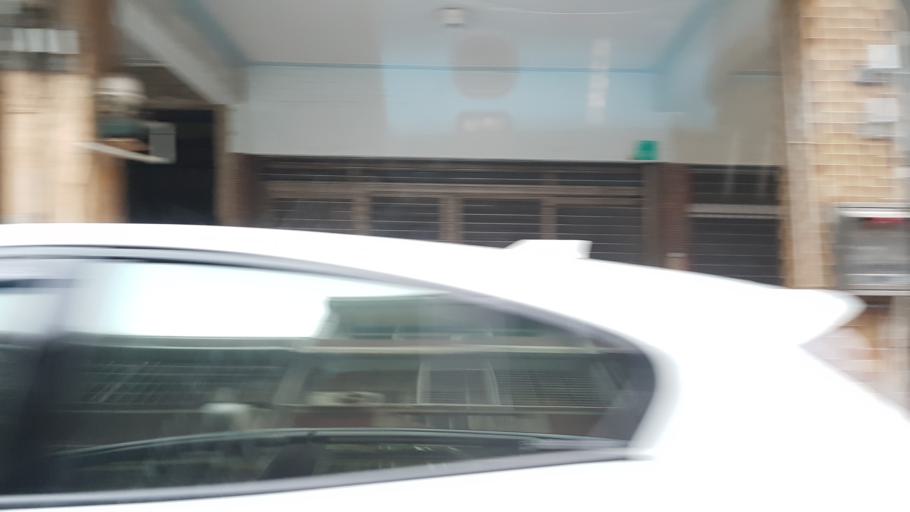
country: TW
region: Taiwan
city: Xinying
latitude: 23.3174
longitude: 120.3129
